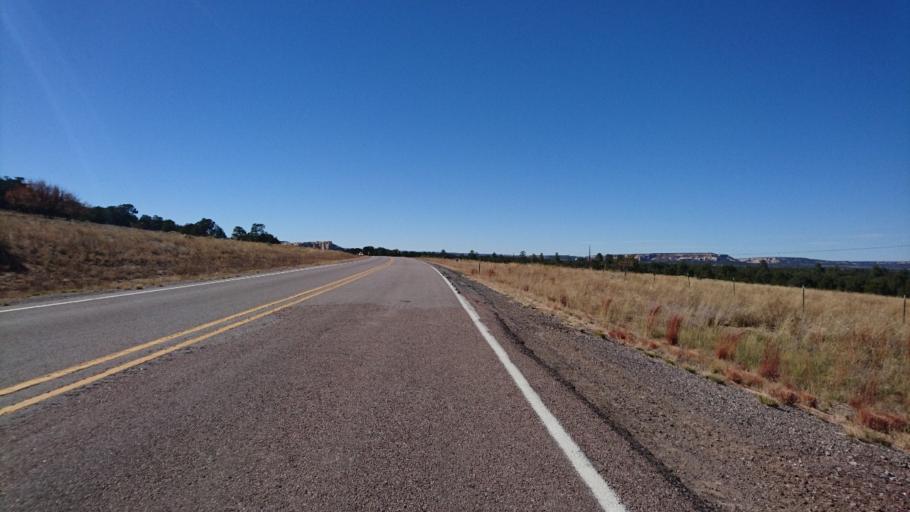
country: US
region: New Mexico
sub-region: McKinley County
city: Thoreau
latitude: 35.0454
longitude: -108.3134
